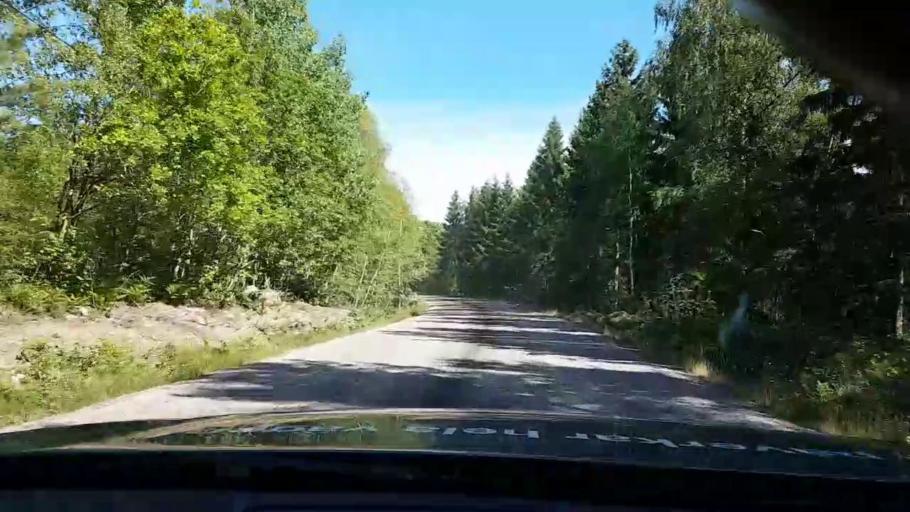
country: SE
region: Kalmar
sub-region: Vasterviks Kommun
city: Vaestervik
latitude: 57.9099
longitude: 16.6454
